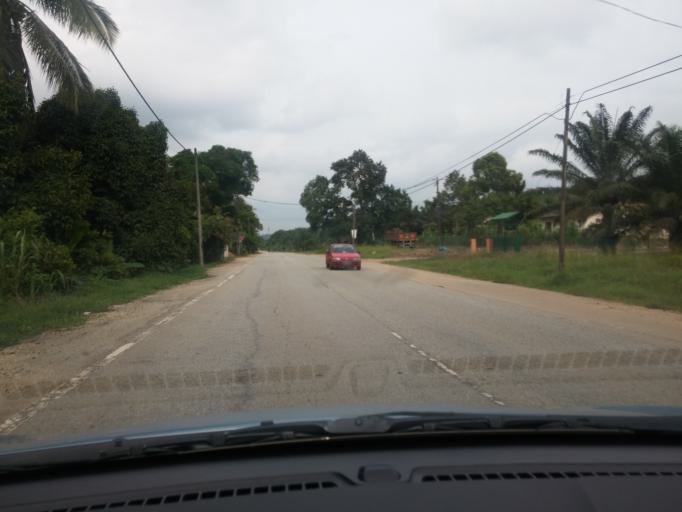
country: MY
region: Pahang
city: Kuantan
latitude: 3.8832
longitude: 103.1659
